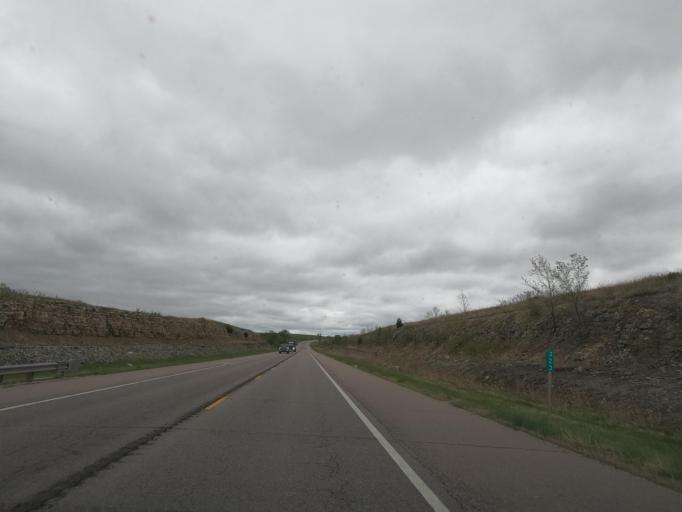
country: US
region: Kansas
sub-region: Greenwood County
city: Eureka
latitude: 37.6547
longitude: -96.4691
